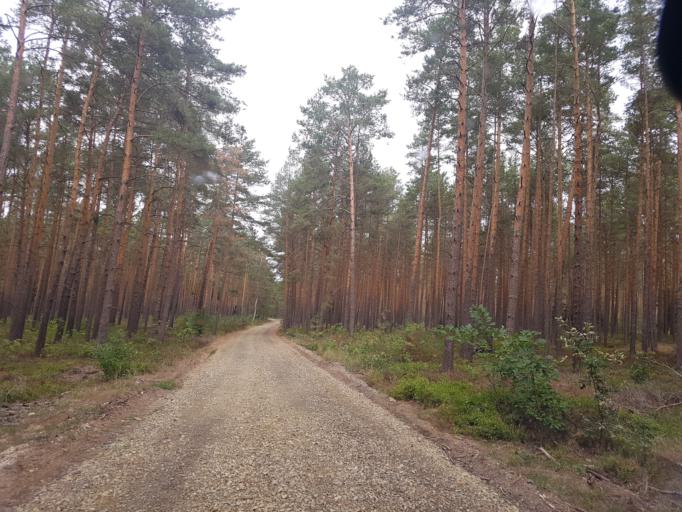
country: DE
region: Brandenburg
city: Schonborn
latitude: 51.5729
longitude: 13.4764
